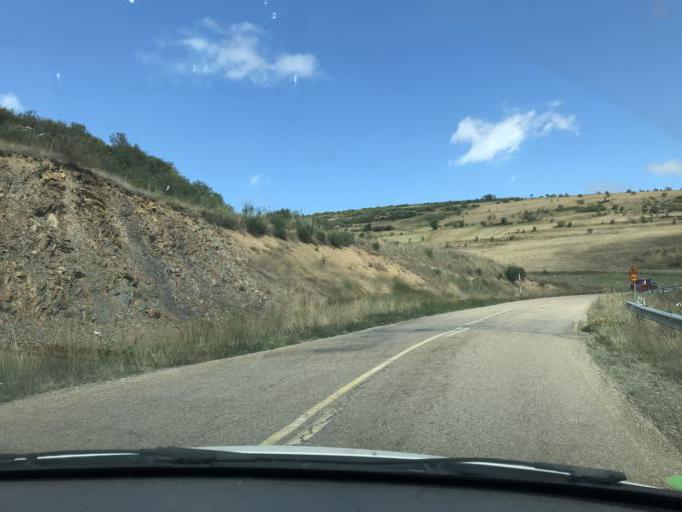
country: ES
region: Castille and Leon
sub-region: Provincia de Palencia
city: Polentinos
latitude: 43.0126
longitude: -4.4963
